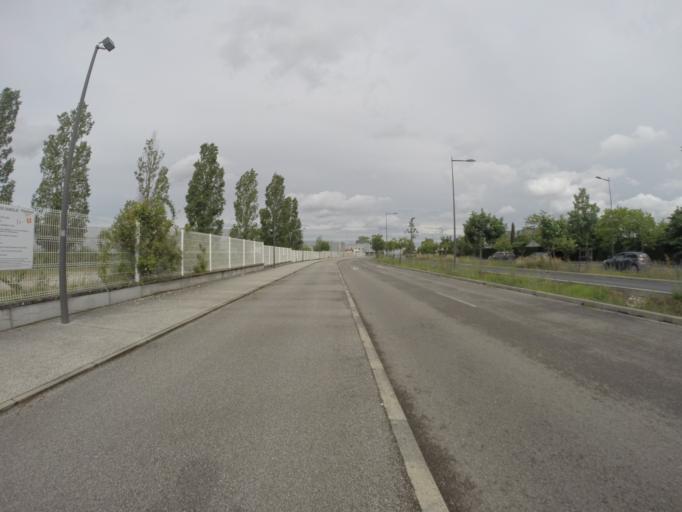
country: FR
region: Rhone-Alpes
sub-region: Departement du Rhone
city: Bron
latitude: 45.7499
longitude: 4.9330
